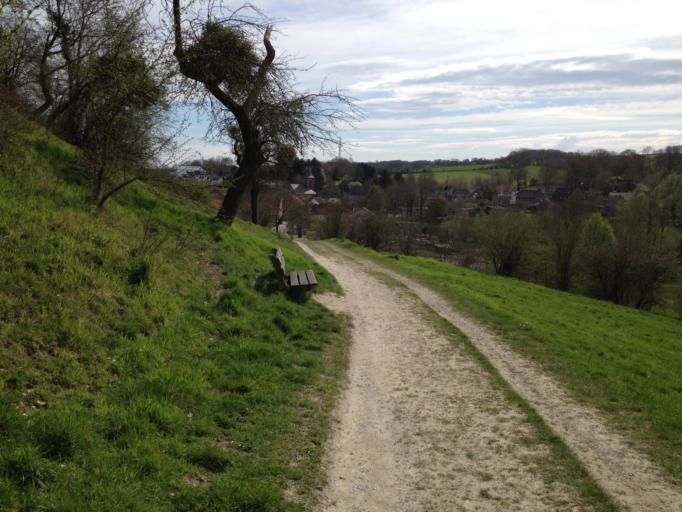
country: BE
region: Flanders
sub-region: Provincie Limburg
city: Sint-Pieters-Voeren
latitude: 50.7719
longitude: 5.8628
